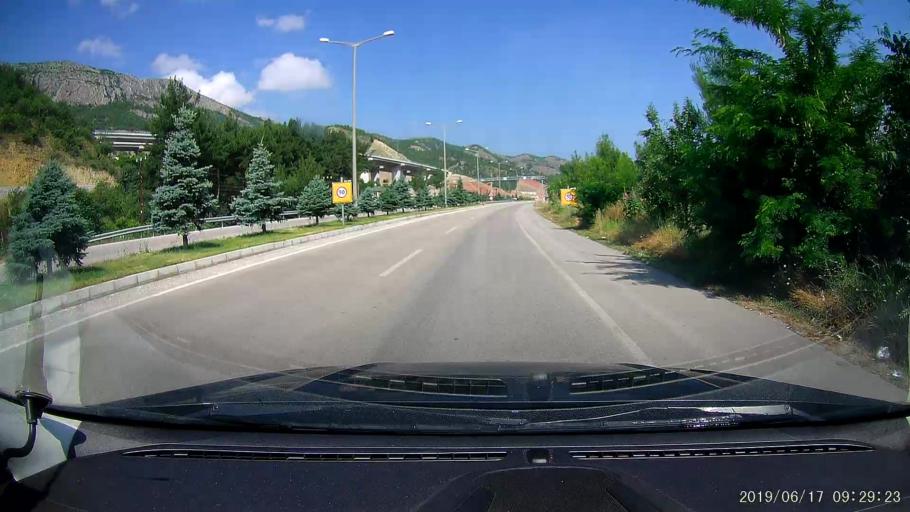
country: TR
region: Amasya
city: Amasya
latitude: 40.6962
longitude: 35.8128
